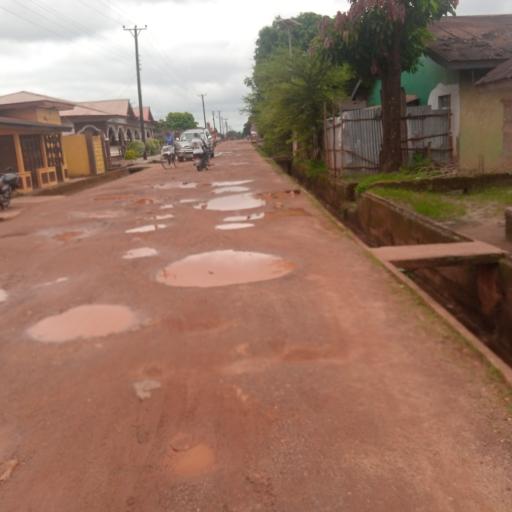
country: SL
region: Eastern Province
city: Kenema
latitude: 7.8847
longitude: -11.1868
